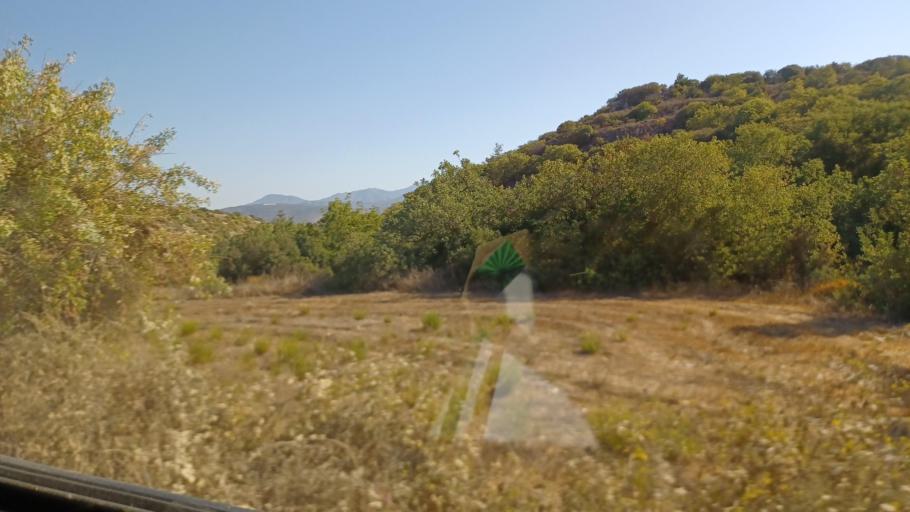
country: CY
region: Pafos
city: Polis
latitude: 34.9597
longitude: 32.4289
